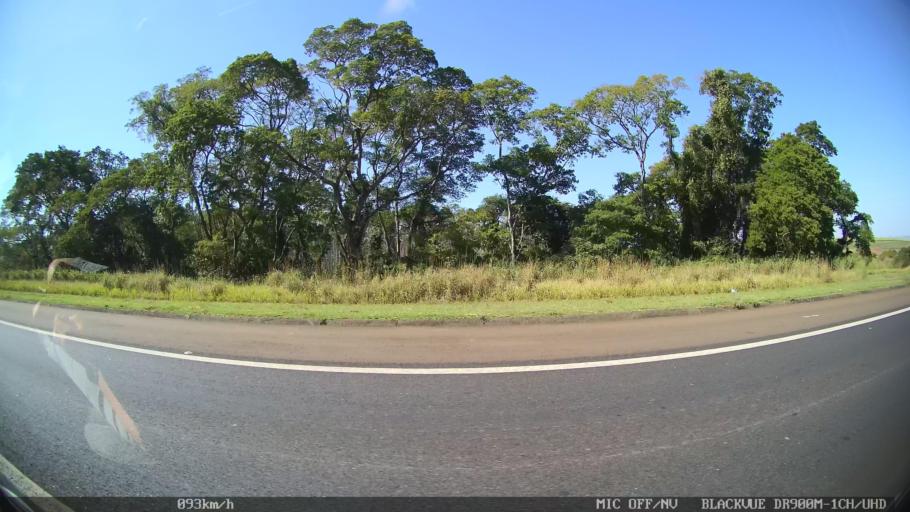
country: BR
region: Sao Paulo
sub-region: Franca
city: Franca
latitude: -20.6934
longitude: -47.4986
